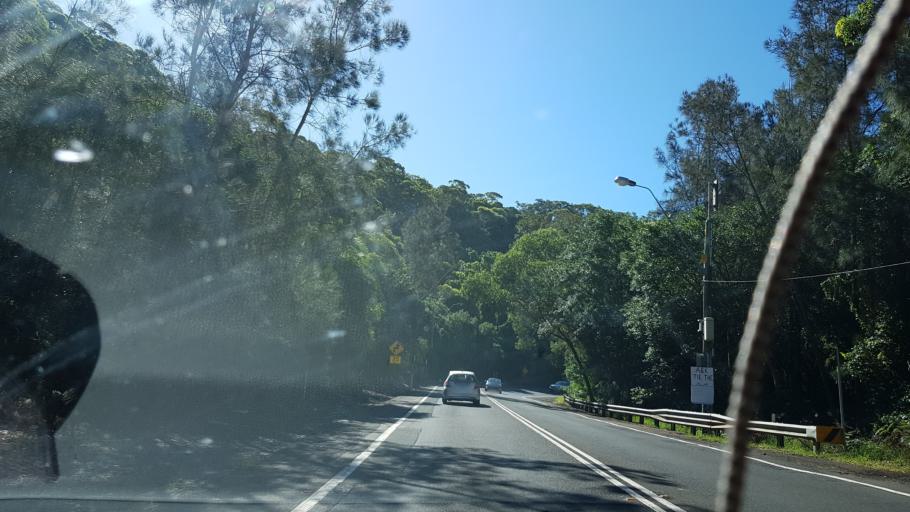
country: AU
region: New South Wales
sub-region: Pittwater
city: Bilgola Beach
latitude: -33.6455
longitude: 151.3239
